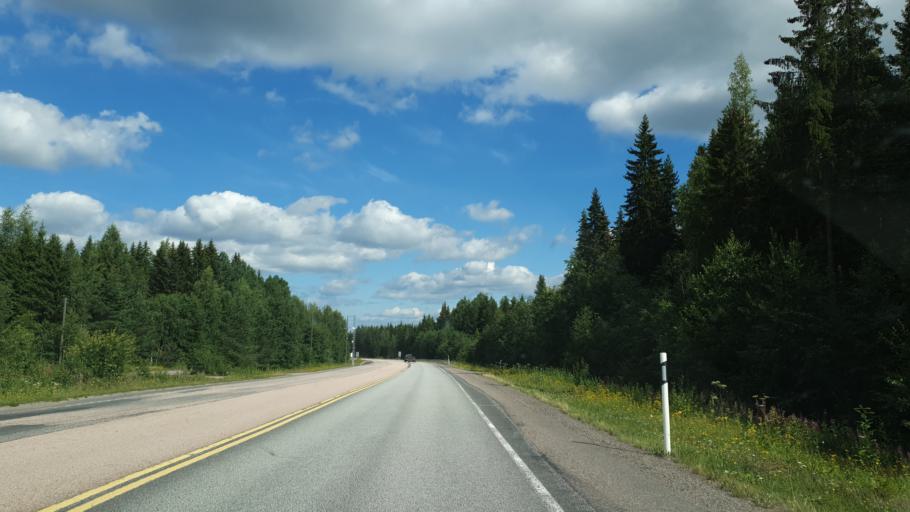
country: FI
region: Central Finland
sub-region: Jaemsae
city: Jaemsae
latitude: 61.8254
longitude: 25.0655
